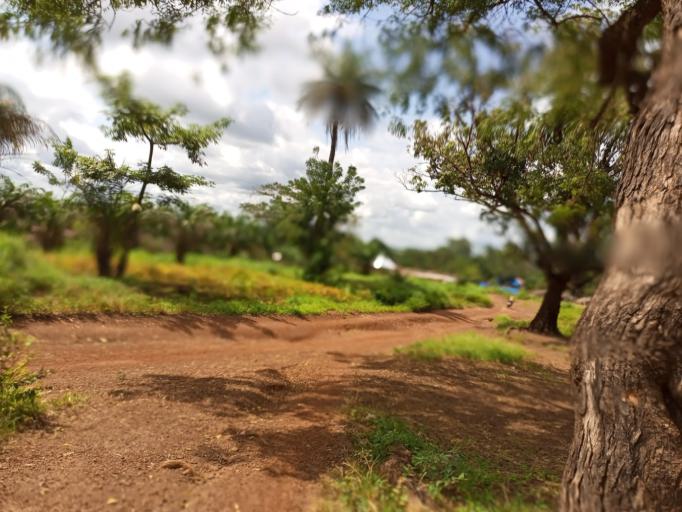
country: SL
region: Northern Province
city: Kamakwie
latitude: 9.5002
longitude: -12.2368
